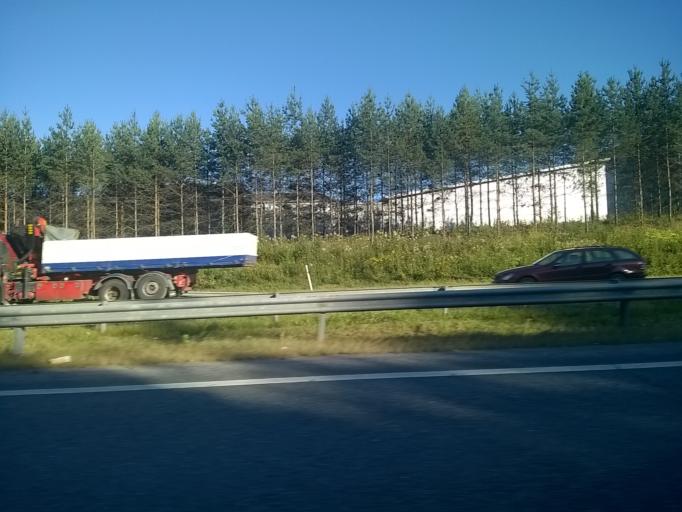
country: FI
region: Pirkanmaa
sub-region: Tampere
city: Tampere
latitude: 61.4730
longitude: 23.8654
